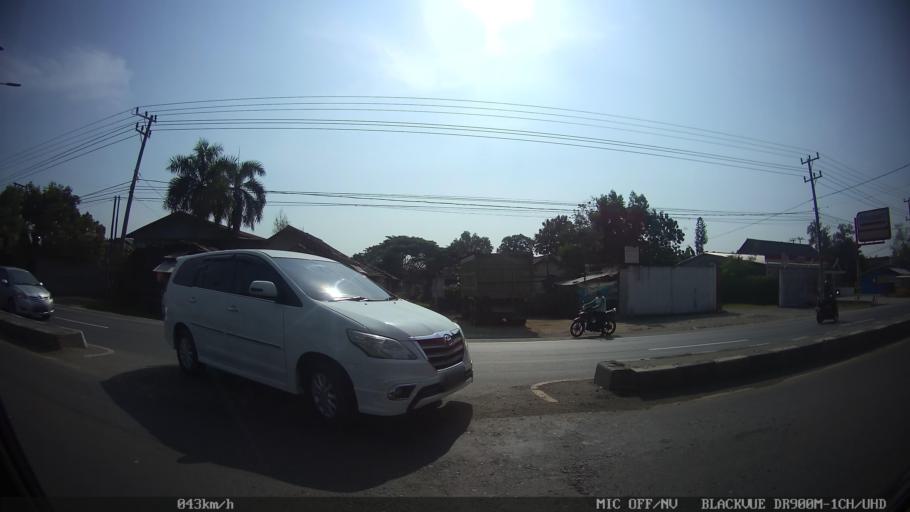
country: ID
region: Lampung
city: Natar
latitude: -5.2701
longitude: 105.1864
